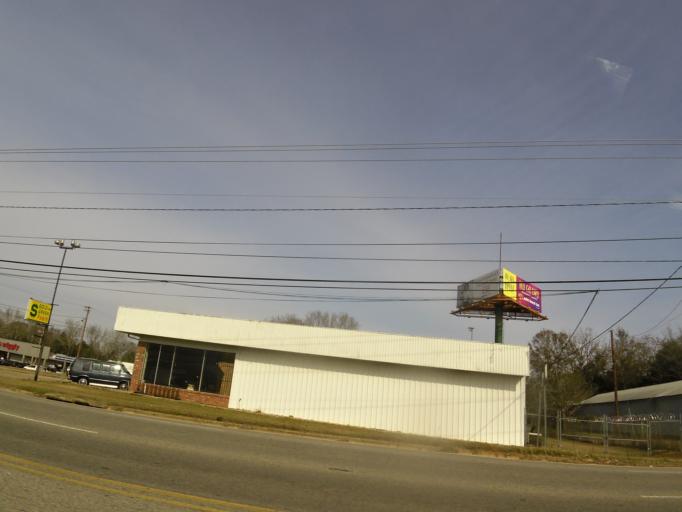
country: US
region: Alabama
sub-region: Houston County
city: Dothan
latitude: 31.2374
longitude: -85.3982
